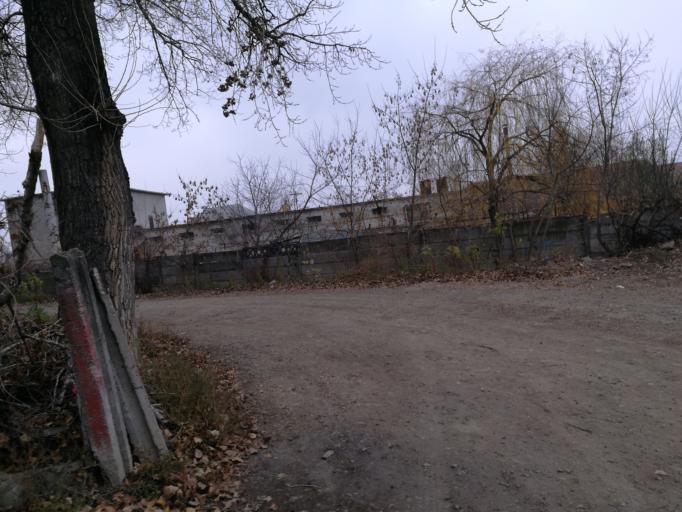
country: RO
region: Suceava
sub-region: Comuna Scheia
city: Scheia
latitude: 47.6727
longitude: 26.2699
